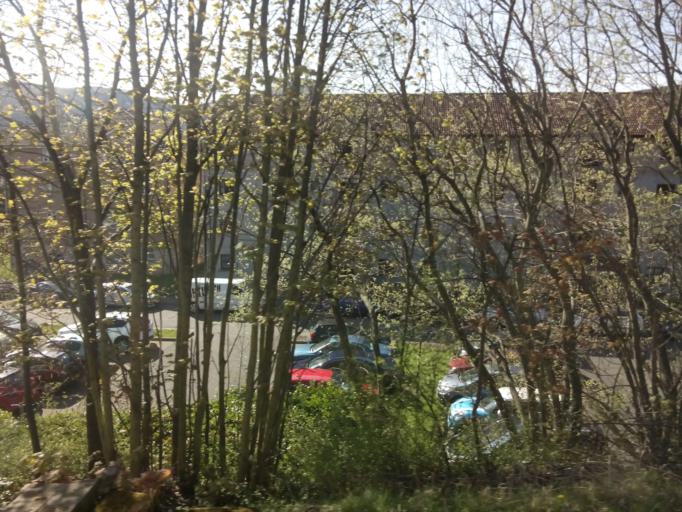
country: GB
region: Scotland
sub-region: West Lothian
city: Seafield
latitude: 55.9554
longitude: -3.1703
